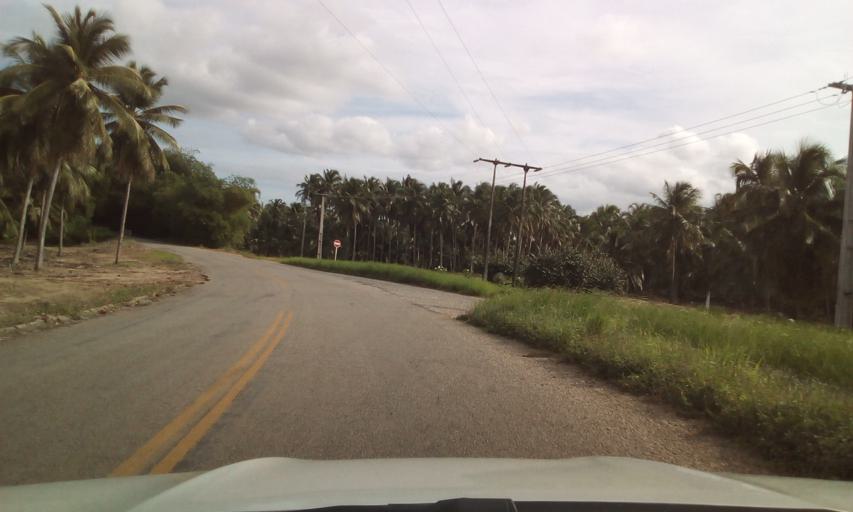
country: BR
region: Paraiba
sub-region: Cabedelo
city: Cabedelo
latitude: -6.9551
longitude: -34.9409
